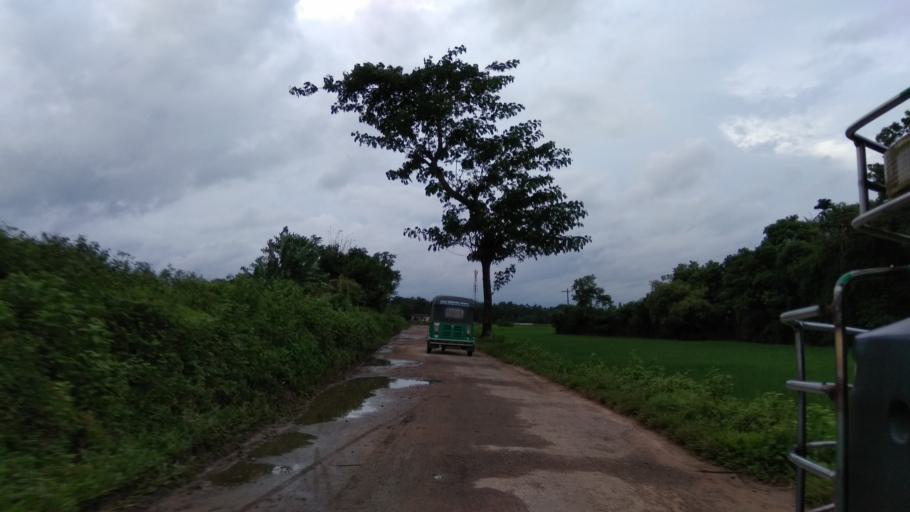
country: IN
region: Tripura
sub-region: Dhalai
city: Kamalpur
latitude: 24.2112
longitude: 91.8597
